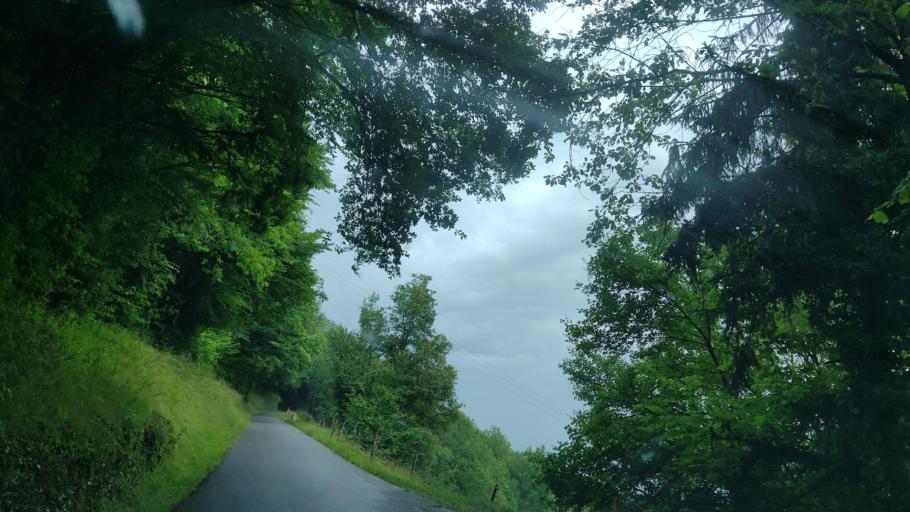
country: FR
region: Rhone-Alpes
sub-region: Departement de la Savoie
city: La Rochette
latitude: 45.4869
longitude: 6.1316
